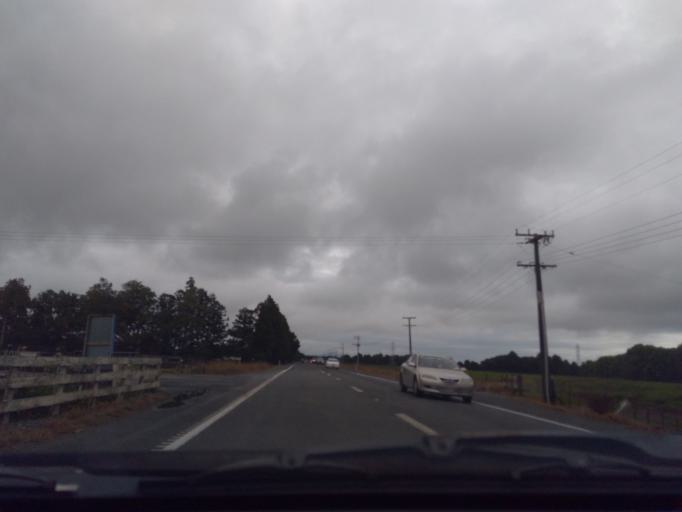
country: NZ
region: Northland
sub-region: Whangarei
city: Ruakaka
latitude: -35.9974
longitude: 174.4180
